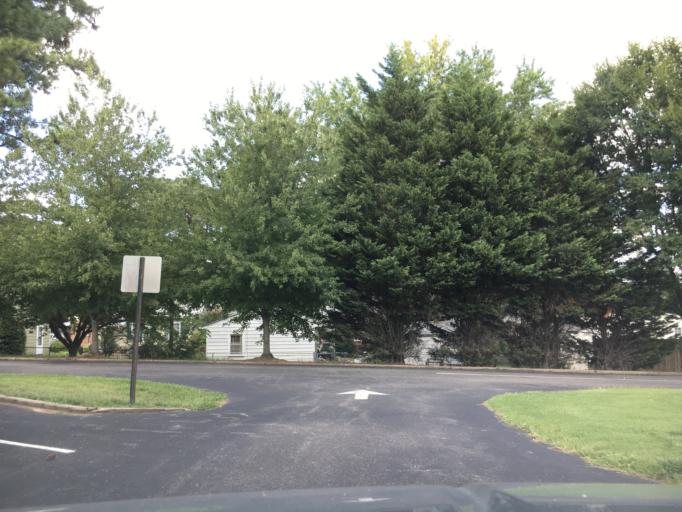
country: US
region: Virginia
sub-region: Henrico County
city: Tuckahoe
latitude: 37.5965
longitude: -77.5310
